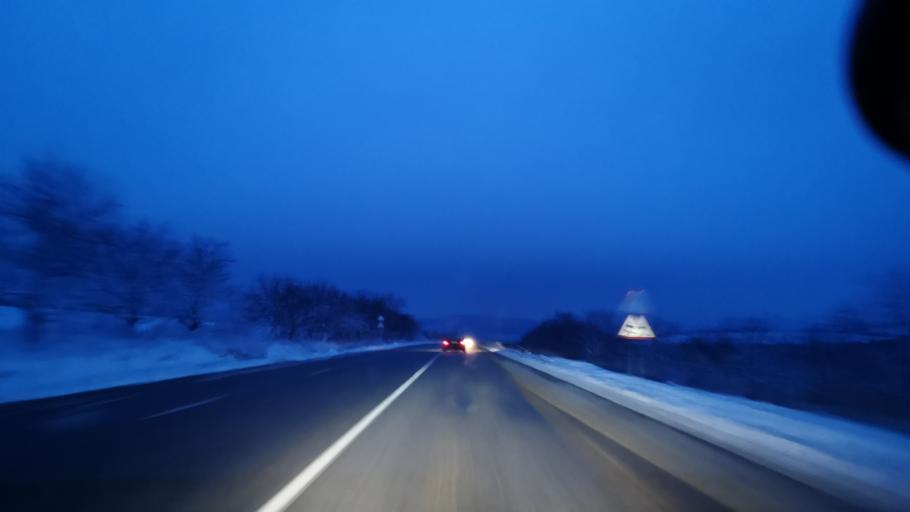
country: MD
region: Orhei
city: Orhei
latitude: 47.5333
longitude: 28.7940
